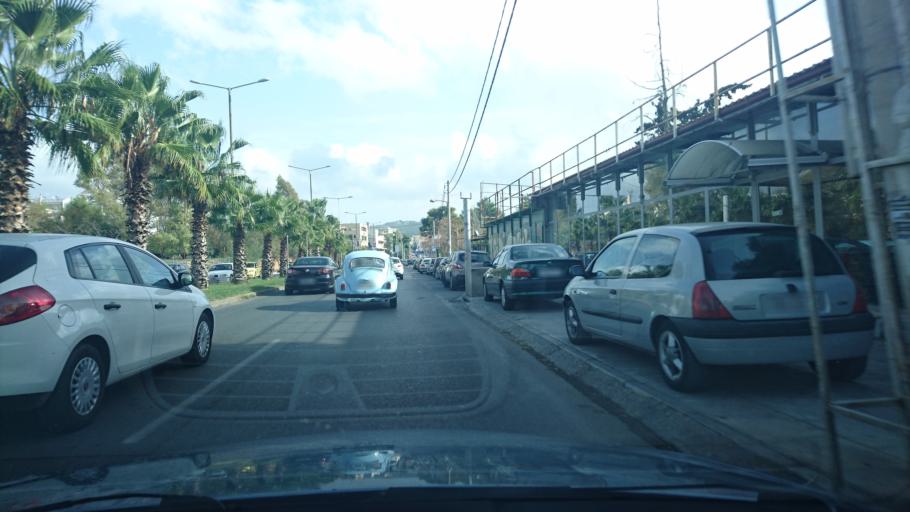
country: GR
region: Attica
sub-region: Nomarchia Athinas
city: Khalandrion
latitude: 38.0162
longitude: 23.8138
